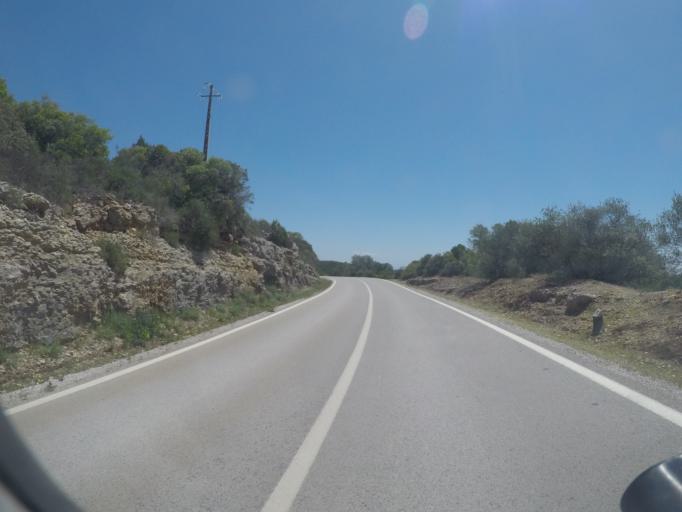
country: PT
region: Setubal
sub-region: Sesimbra
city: Sesimbra
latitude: 38.4611
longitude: -9.0249
